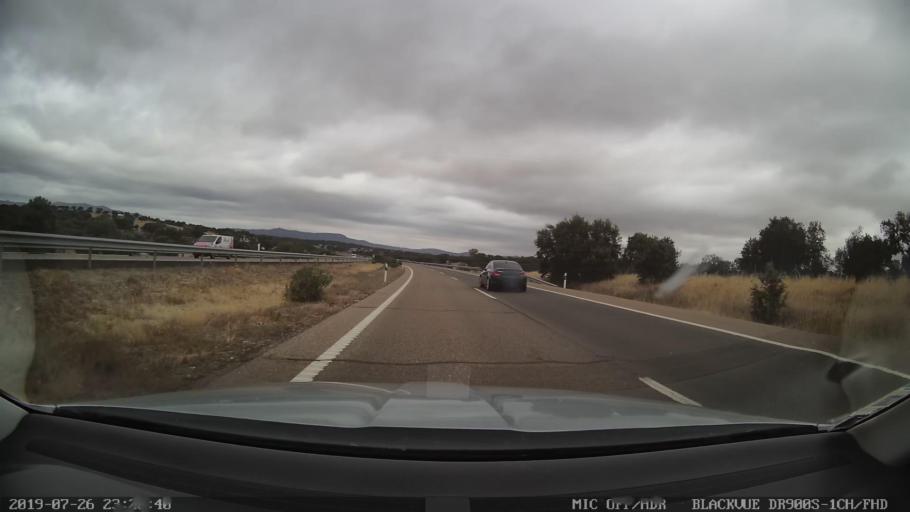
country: ES
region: Extremadura
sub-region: Provincia de Caceres
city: Villamesias
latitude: 39.2122
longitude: -5.8775
